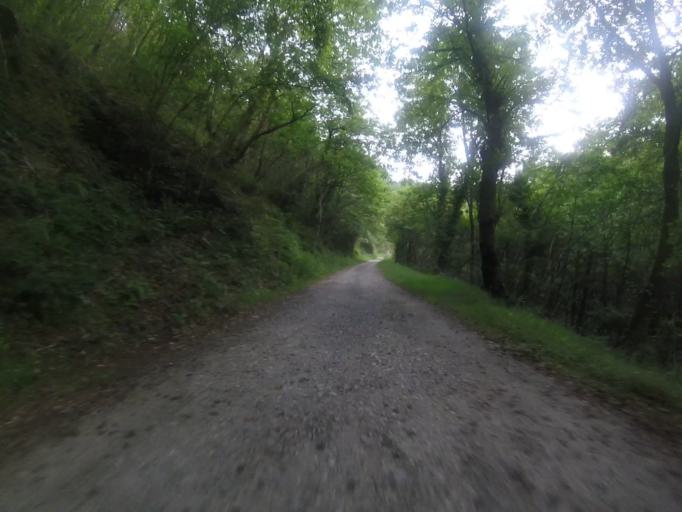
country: ES
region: Basque Country
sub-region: Provincia de Guipuzcoa
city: Berastegui
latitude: 43.1253
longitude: -1.9350
